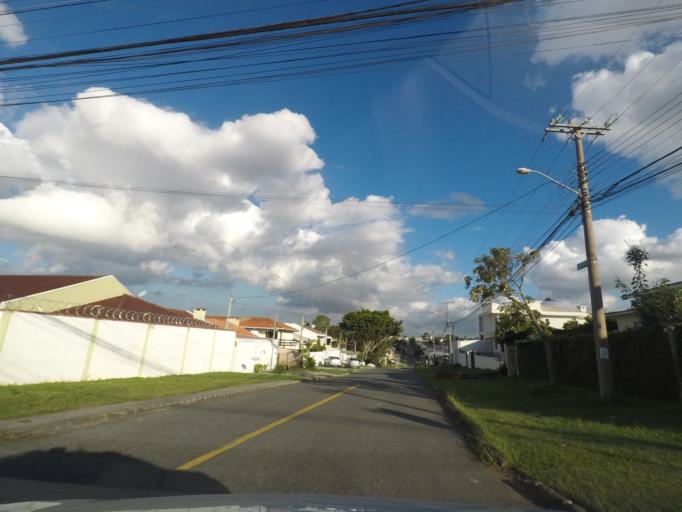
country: BR
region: Parana
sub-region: Sao Jose Dos Pinhais
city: Sao Jose dos Pinhais
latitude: -25.4935
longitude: -49.2567
